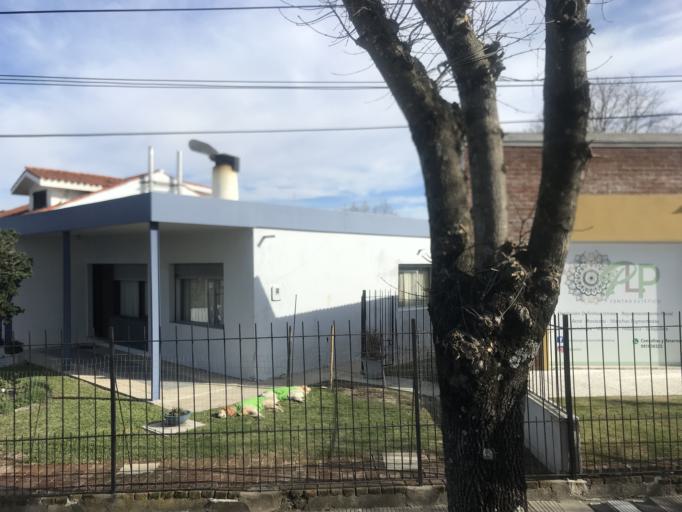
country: UY
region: Colonia
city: Colonia del Sacramento
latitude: -34.4682
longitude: -57.8384
